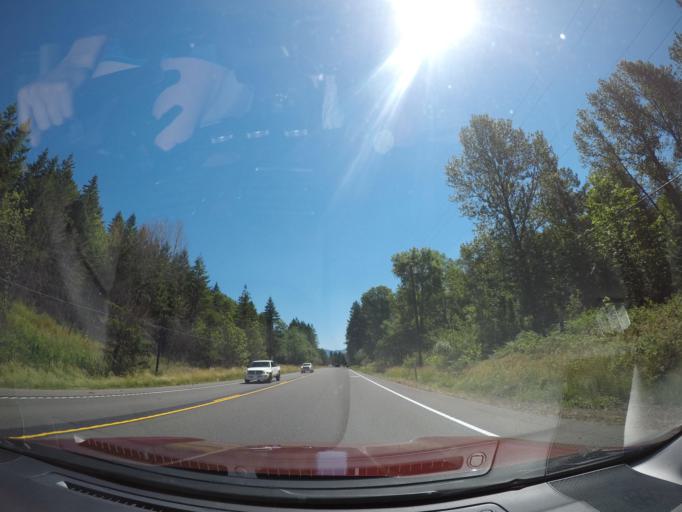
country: US
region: Oregon
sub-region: Linn County
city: Mill City
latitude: 44.7568
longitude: -122.4459
